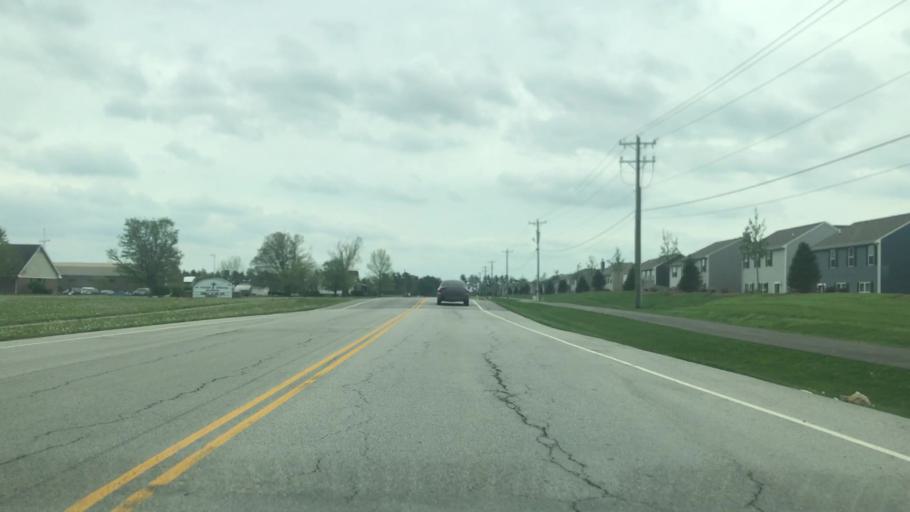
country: US
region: Indiana
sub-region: Johnson County
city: New Whiteland
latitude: 39.5852
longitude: -86.0830
